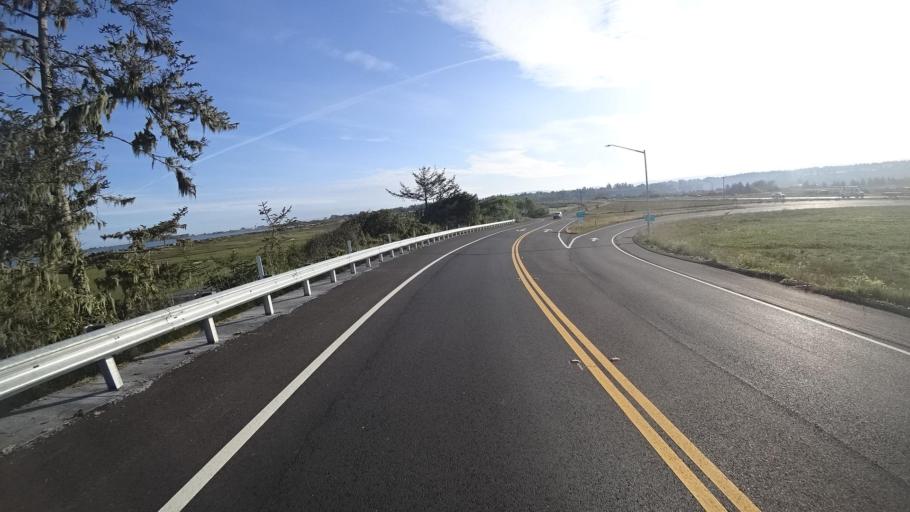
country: US
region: California
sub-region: Humboldt County
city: Humboldt Hill
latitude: 40.7468
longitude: -124.1999
